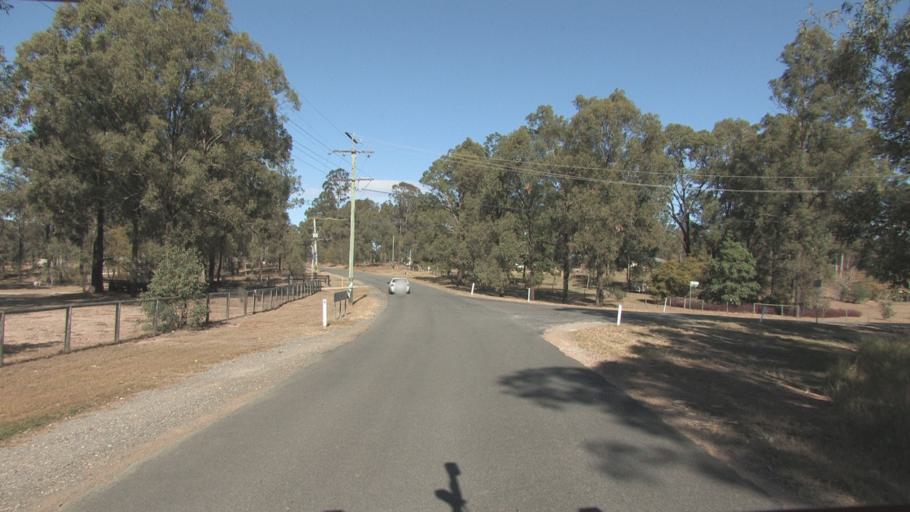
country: AU
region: Queensland
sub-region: Logan
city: Cedar Vale
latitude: -27.8566
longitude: 152.9915
